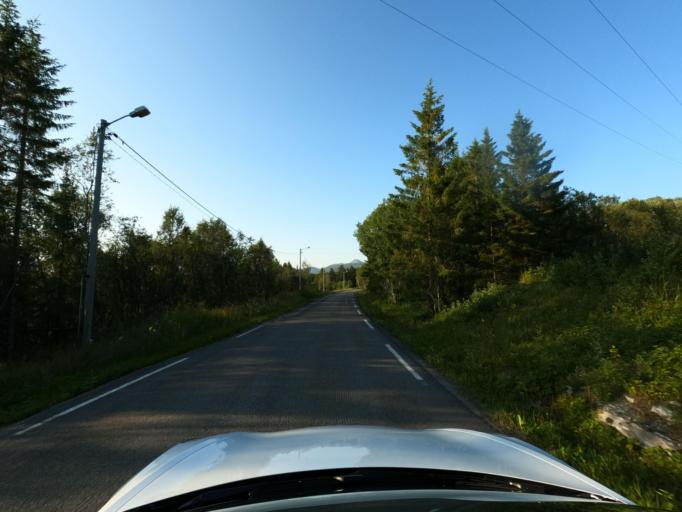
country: NO
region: Nordland
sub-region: Ballangen
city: Ballangen
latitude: 68.4953
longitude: 16.7345
